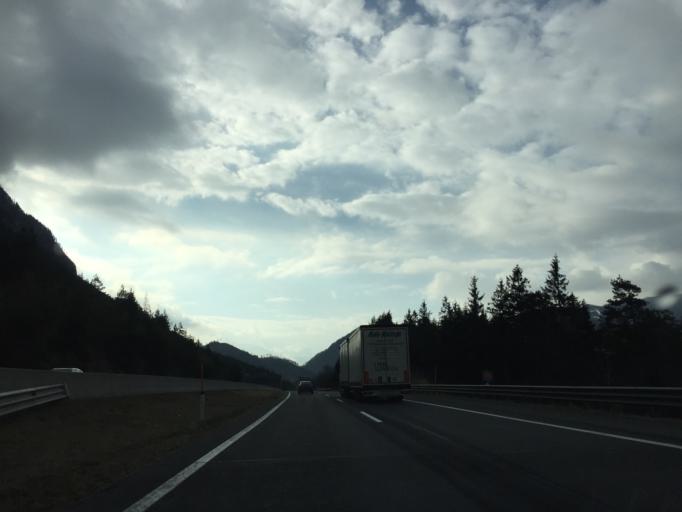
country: AT
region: Salzburg
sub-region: Politischer Bezirk Sankt Johann im Pongau
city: Werfen
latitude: 47.5152
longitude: 13.1701
